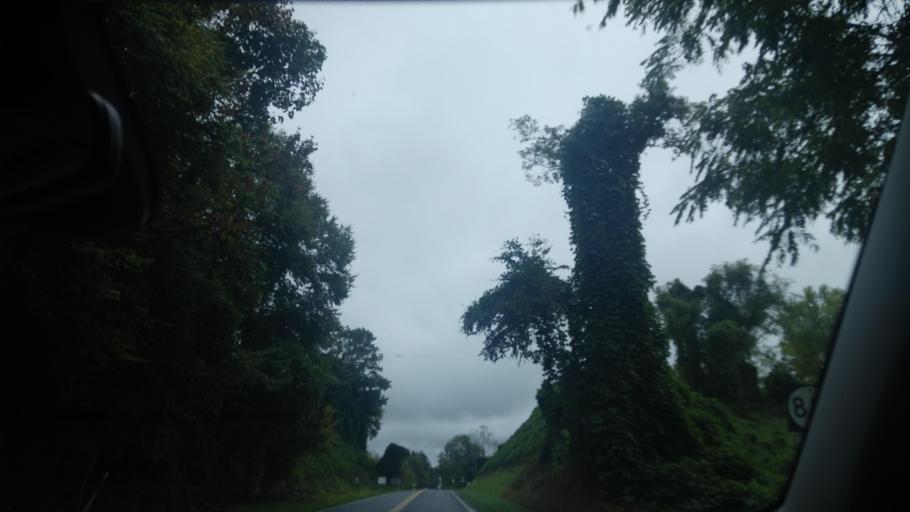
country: US
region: Virginia
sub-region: City of Galax
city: Galax
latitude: 36.6271
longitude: -80.9211
